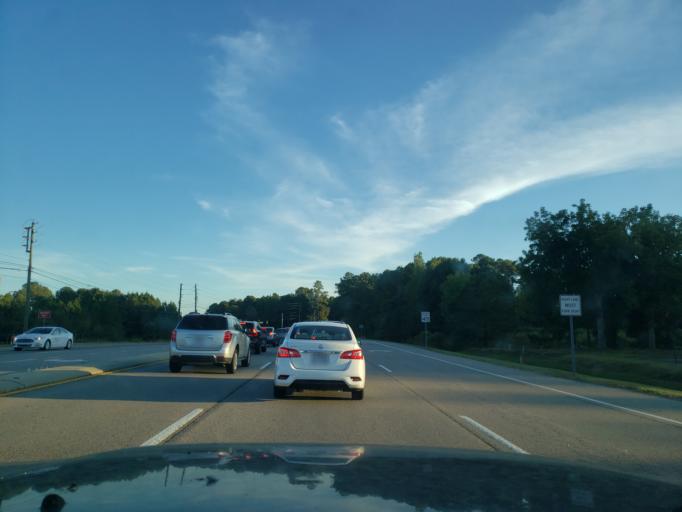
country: US
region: North Carolina
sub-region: Wake County
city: Morrisville
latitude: 35.8305
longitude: -78.8533
